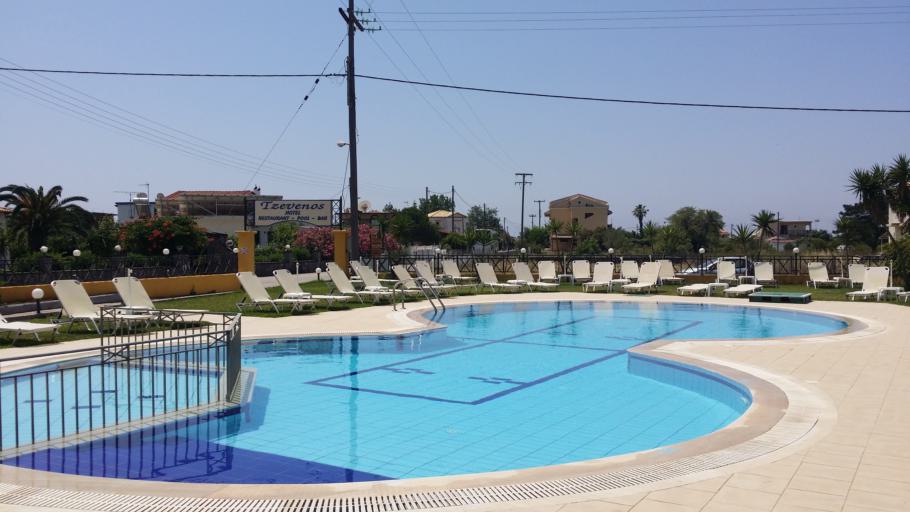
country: GR
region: Ionian Islands
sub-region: Nomos Kerkyras
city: Perivoli
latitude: 39.4282
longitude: 19.9488
